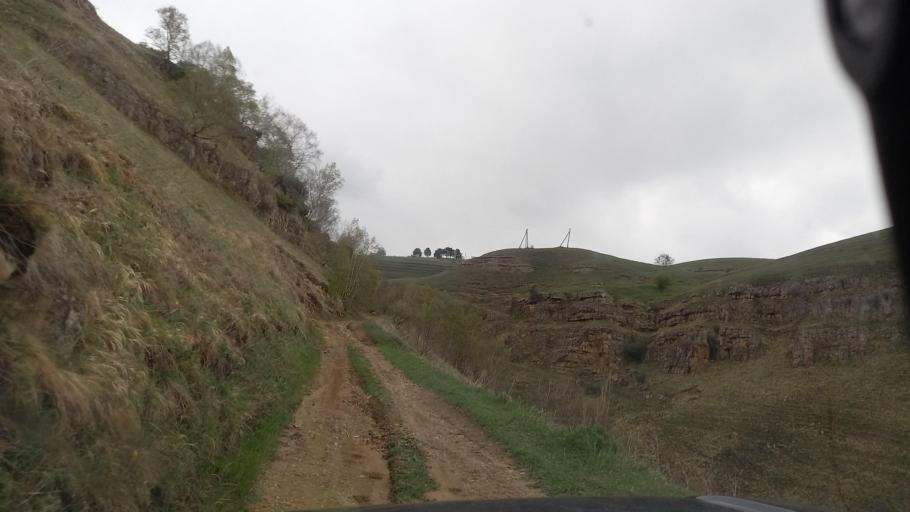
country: RU
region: Stavropol'skiy
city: Nezhinskiy
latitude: 43.8532
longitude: 42.6387
